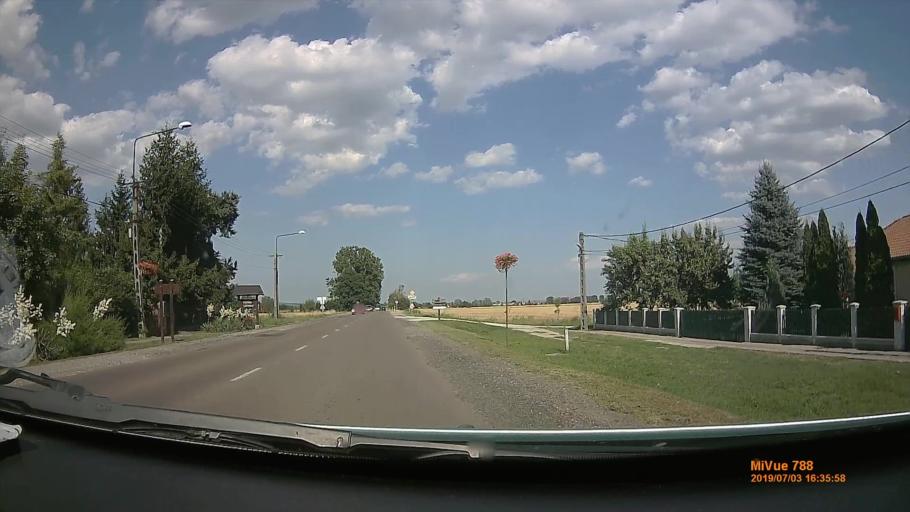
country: HU
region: Borsod-Abauj-Zemplen
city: Sajokaza
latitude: 48.2739
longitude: 20.5608
